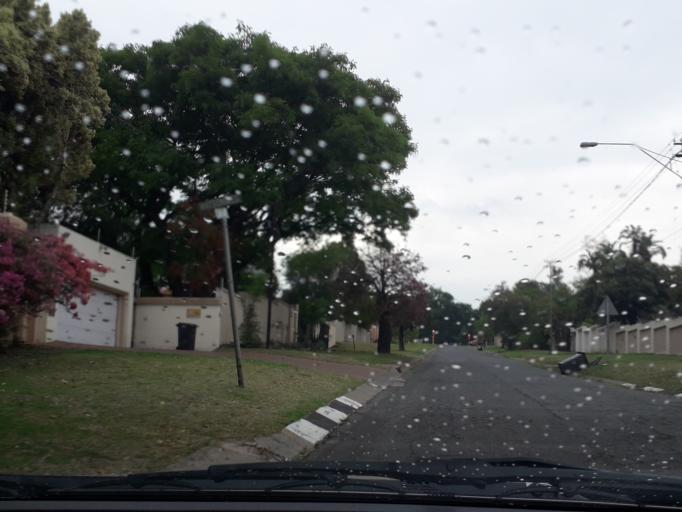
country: ZA
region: Gauteng
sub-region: City of Johannesburg Metropolitan Municipality
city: Modderfontein
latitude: -26.1349
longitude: 28.1038
